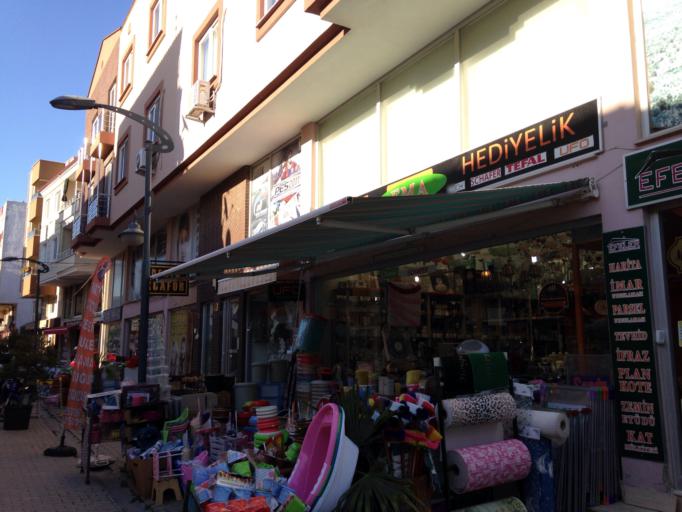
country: TR
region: Canakkale
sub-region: Merkez
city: Kucukkuyu
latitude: 39.5466
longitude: 26.6038
